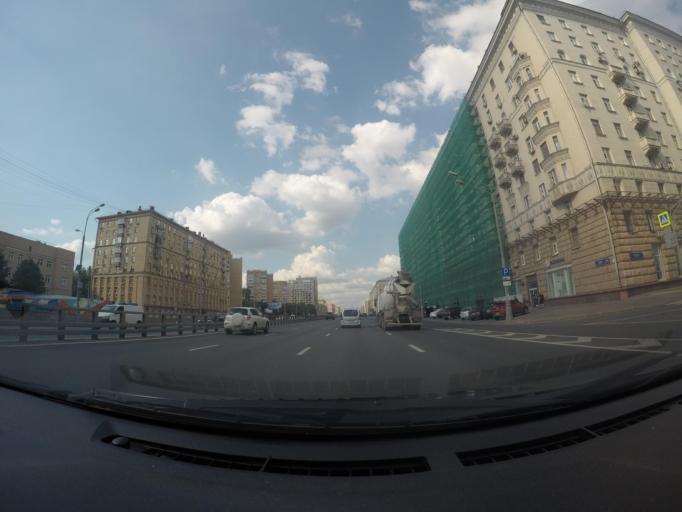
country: RU
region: Moscow
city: Mar'ina Roshcha
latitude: 55.8034
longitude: 37.6363
